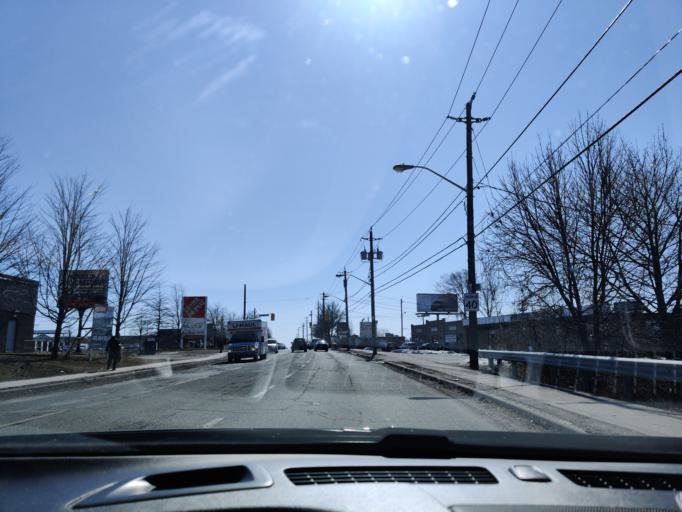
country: CA
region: Ontario
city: Toronto
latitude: 43.7029
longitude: -79.4645
